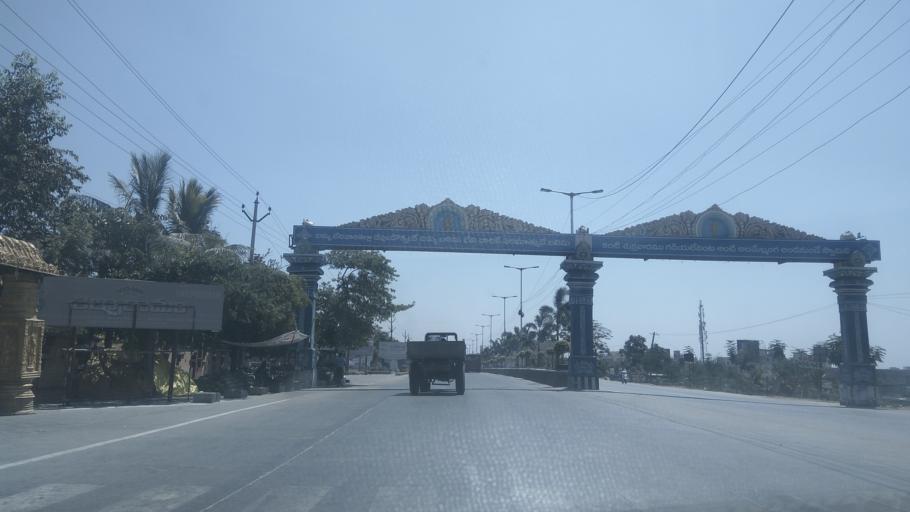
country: IN
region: Andhra Pradesh
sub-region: Chittoor
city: Tirupati
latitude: 13.6126
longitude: 79.4392
